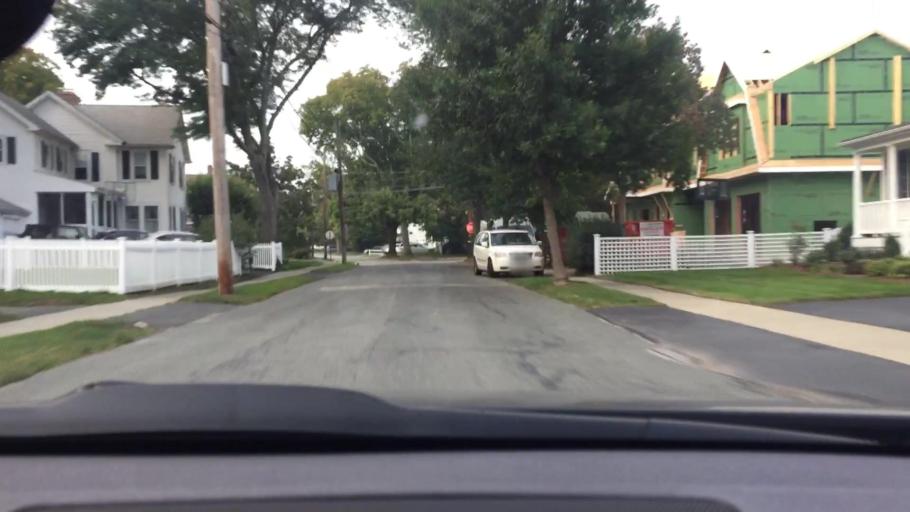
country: US
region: Massachusetts
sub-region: Norfolk County
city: Needham
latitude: 42.2797
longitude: -71.2248
